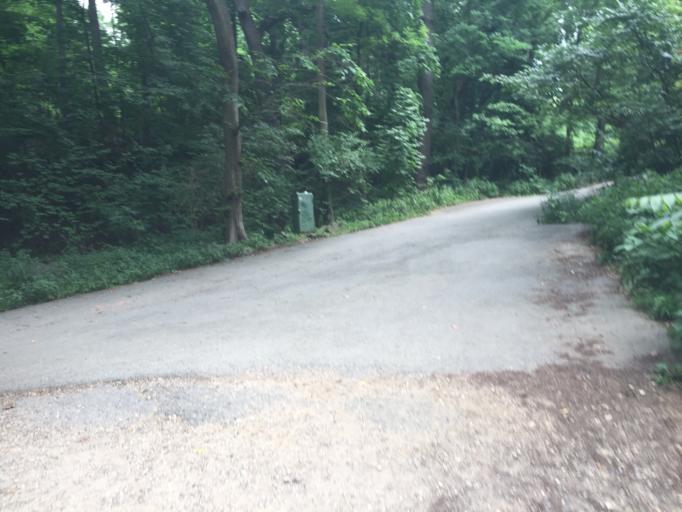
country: US
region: Washington, D.C.
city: Washington, D.C.
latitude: 38.9153
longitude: -77.0616
